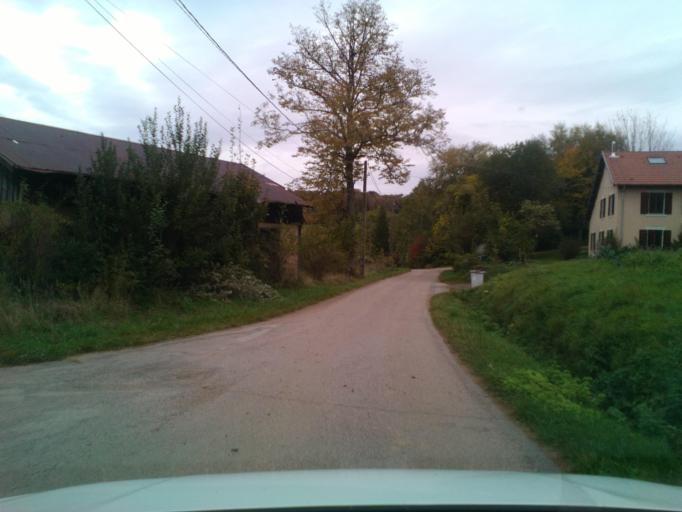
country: FR
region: Lorraine
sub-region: Departement des Vosges
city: Sainte-Marguerite
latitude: 48.3315
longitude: 7.0145
